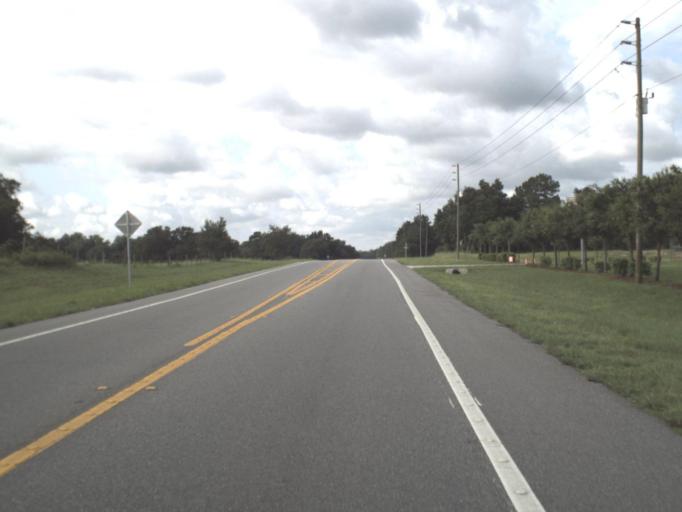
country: US
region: Florida
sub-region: Hernando County
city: Ridge Manor
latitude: 28.5005
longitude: -82.1722
